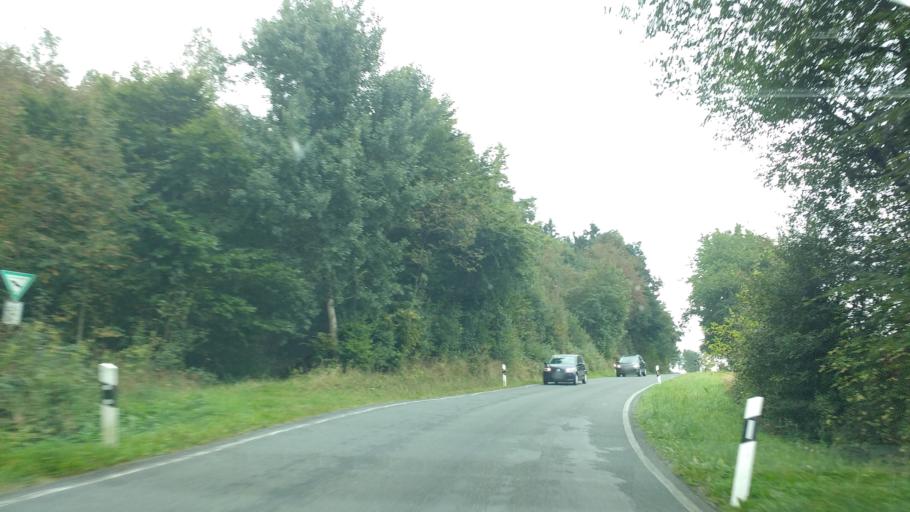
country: DE
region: North Rhine-Westphalia
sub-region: Regierungsbezirk Detmold
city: Horn
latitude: 51.8193
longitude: 8.9447
